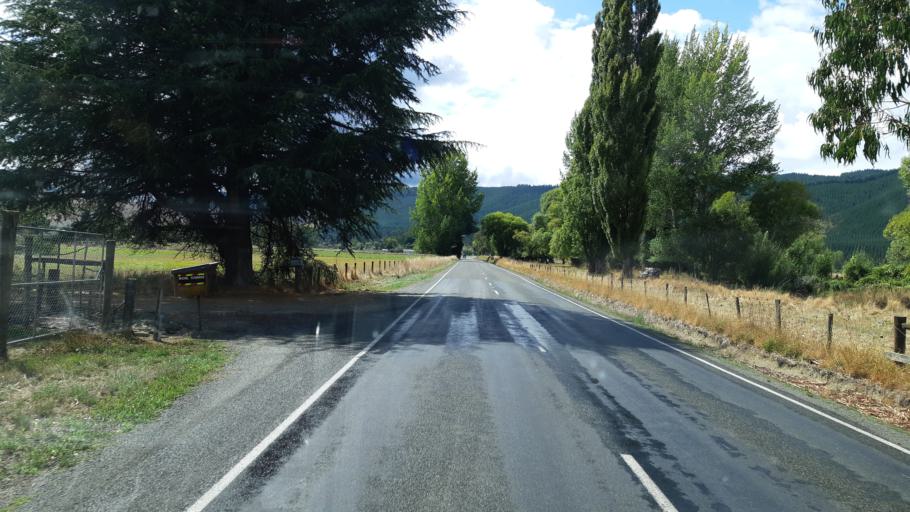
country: NZ
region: Tasman
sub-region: Tasman District
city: Wakefield
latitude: -41.4519
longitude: 172.8222
